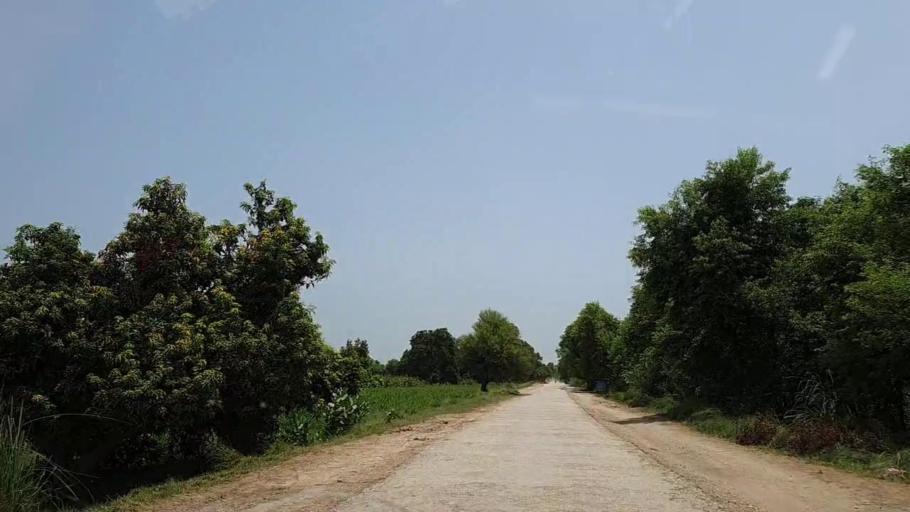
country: PK
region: Sindh
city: Tharu Shah
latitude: 26.9491
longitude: 68.0985
